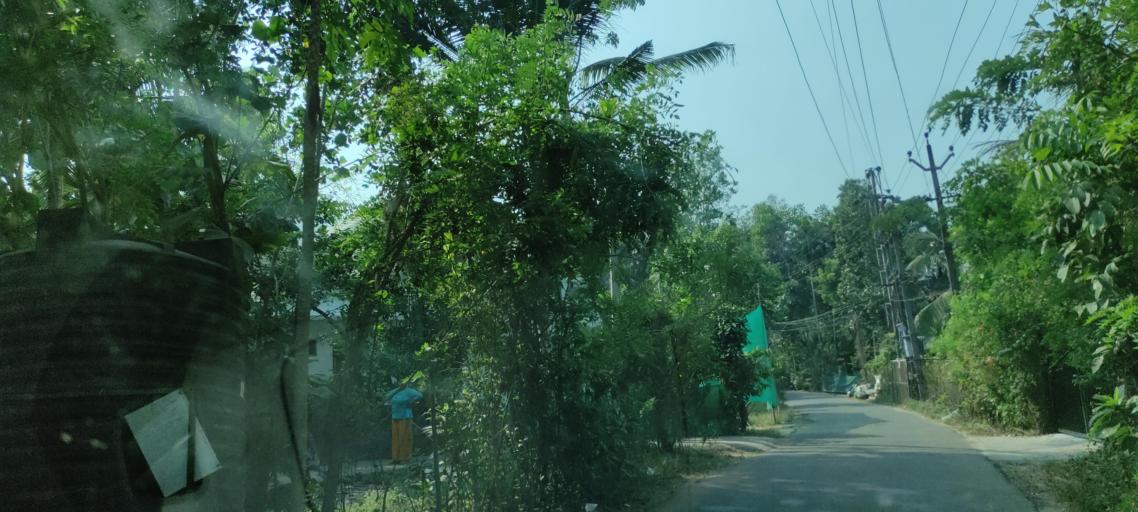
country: IN
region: Kerala
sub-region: Pattanamtitta
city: Tiruvalla
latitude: 9.3559
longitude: 76.5158
